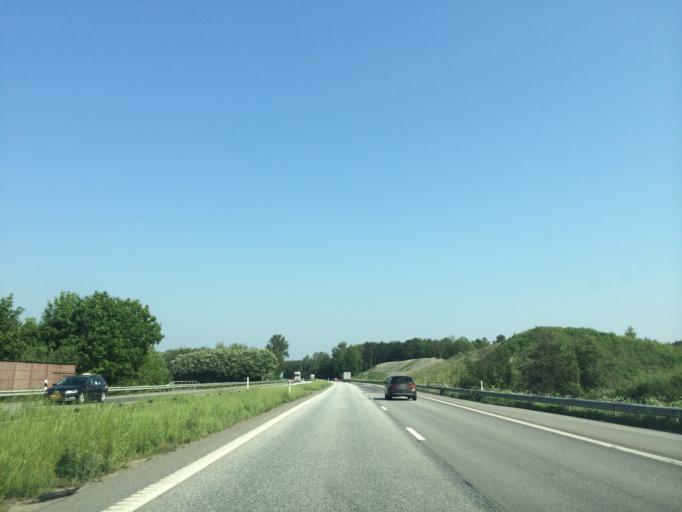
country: SE
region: Skane
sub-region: Landskrona
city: Asmundtorp
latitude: 55.8320
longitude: 12.9284
